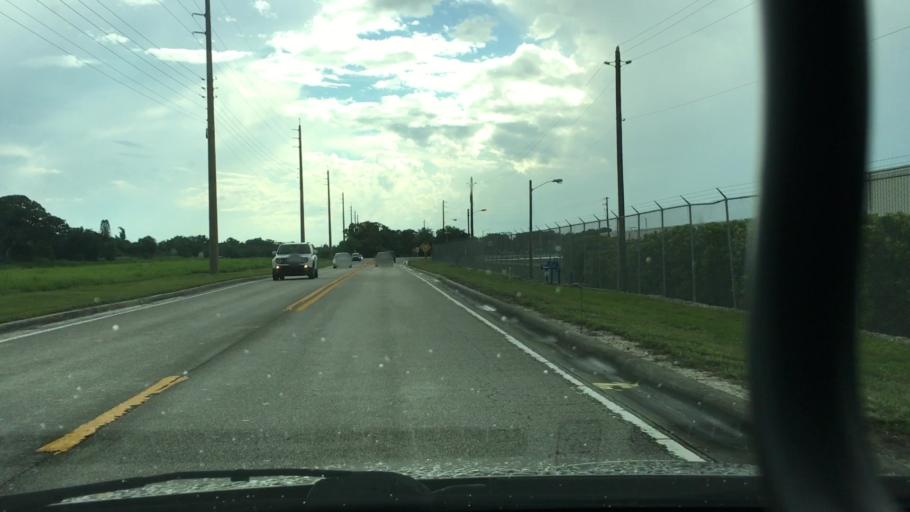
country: US
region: Florida
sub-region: Indian River County
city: Vero Beach
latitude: 27.6469
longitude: -80.4094
